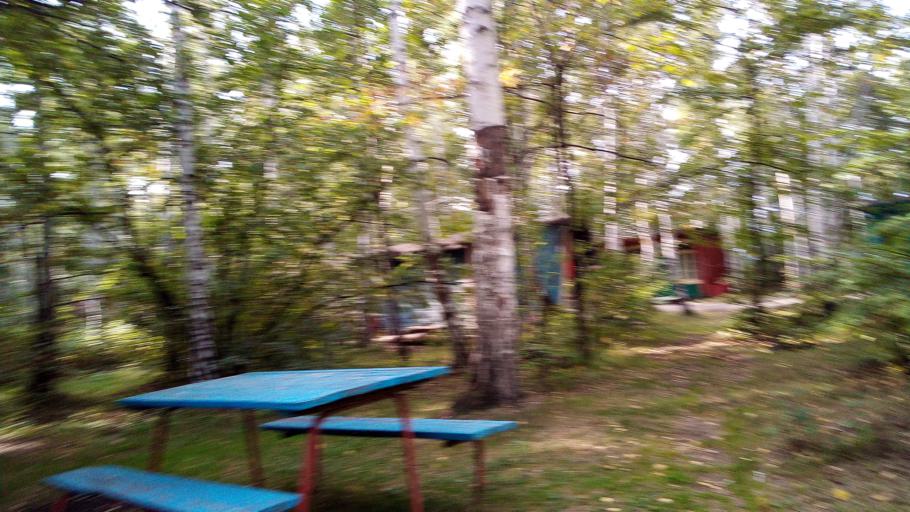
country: RU
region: Chelyabinsk
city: Tayginka
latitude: 55.4785
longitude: 60.4963
